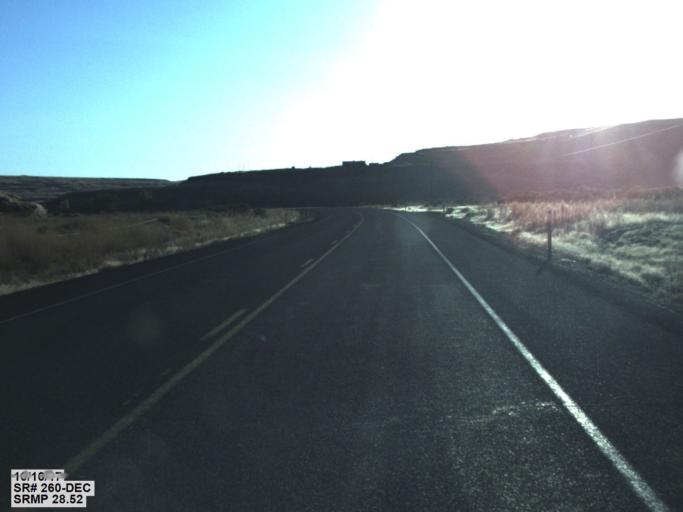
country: US
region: Washington
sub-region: Franklin County
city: Connell
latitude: 46.6621
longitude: -118.4885
